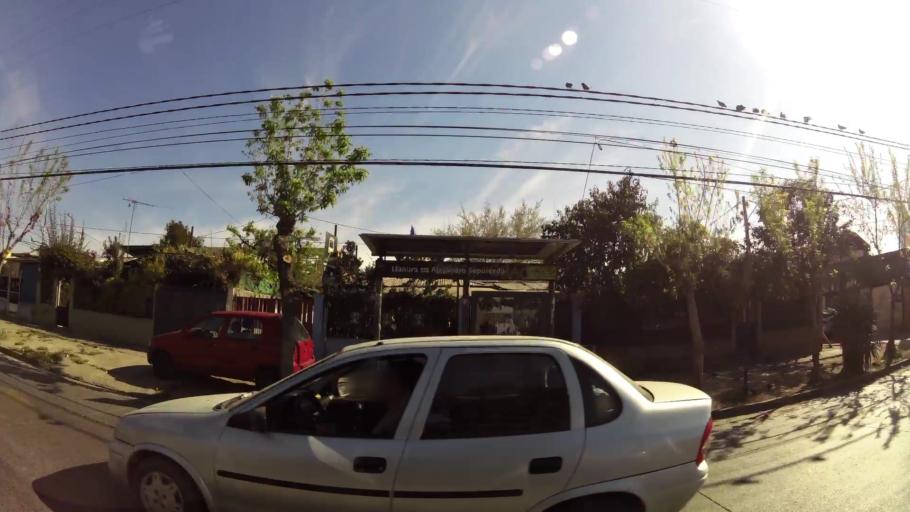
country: CL
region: Santiago Metropolitan
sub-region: Provincia de Santiago
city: Villa Presidente Frei, Nunoa, Santiago, Chile
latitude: -33.4734
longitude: -70.5673
